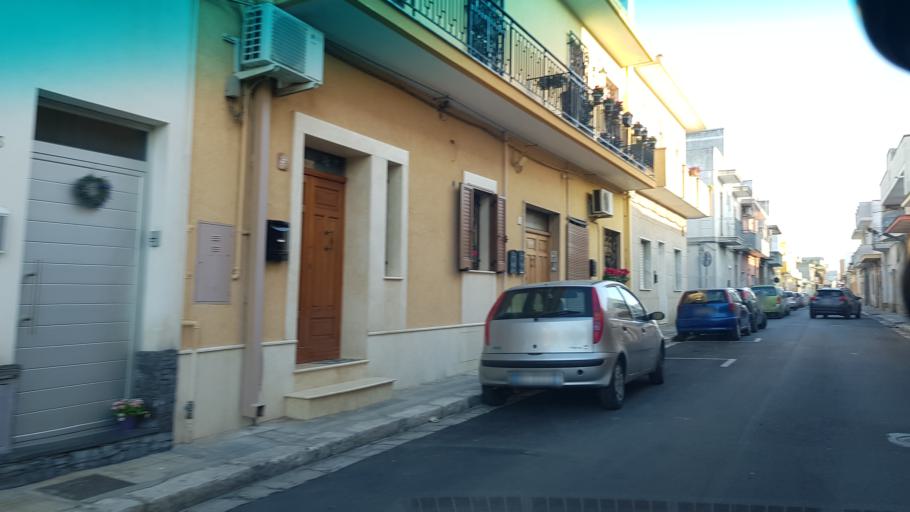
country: IT
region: Apulia
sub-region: Provincia di Brindisi
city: Mesagne
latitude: 40.5555
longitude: 17.8028
